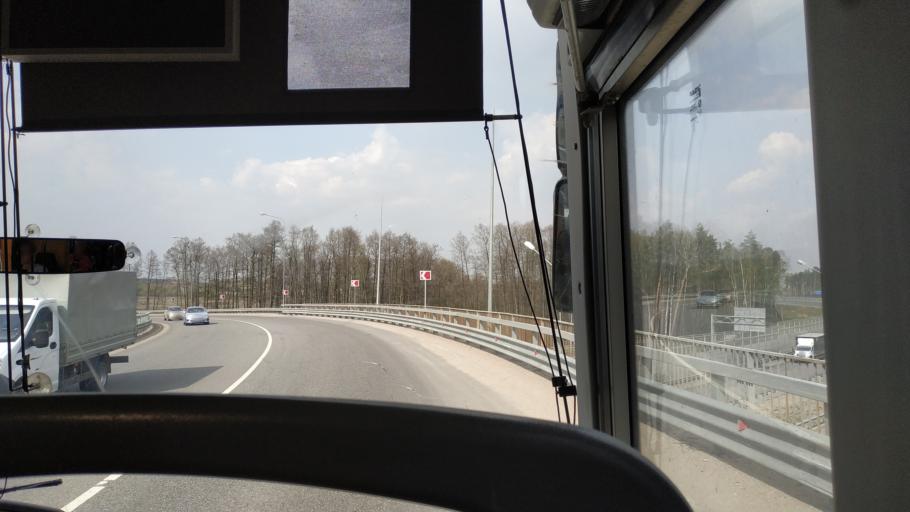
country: RU
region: Moskovskaya
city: Tomilino
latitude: 55.6198
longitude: 37.9294
